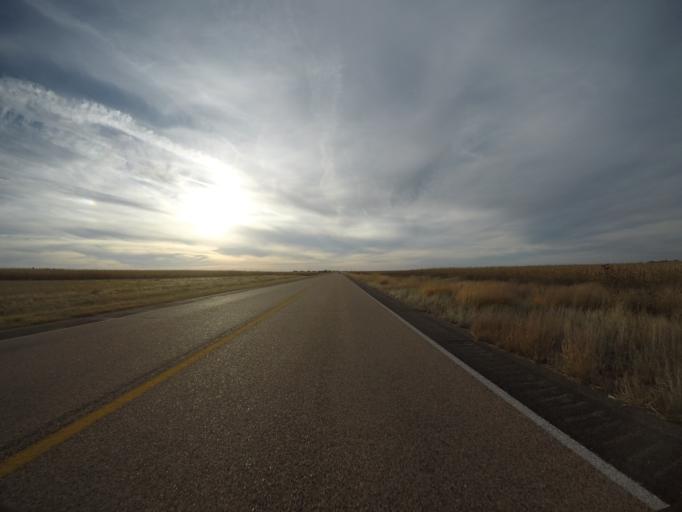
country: US
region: Colorado
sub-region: Kit Carson County
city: Burlington
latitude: 39.6565
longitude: -102.5853
